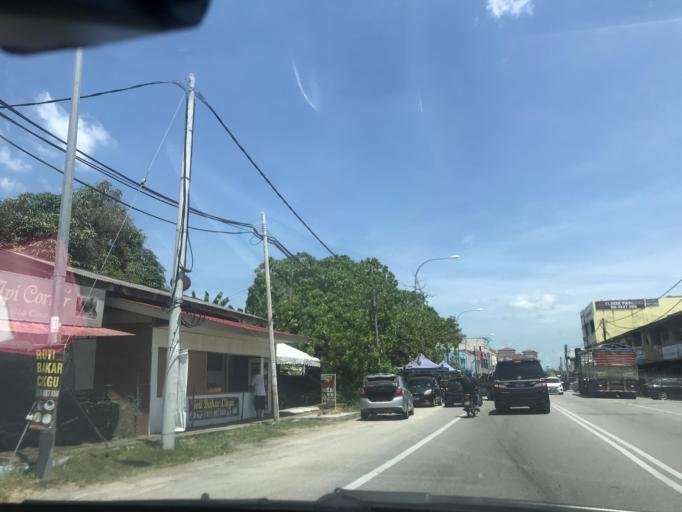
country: MY
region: Kelantan
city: Kota Bharu
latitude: 6.1247
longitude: 102.2509
